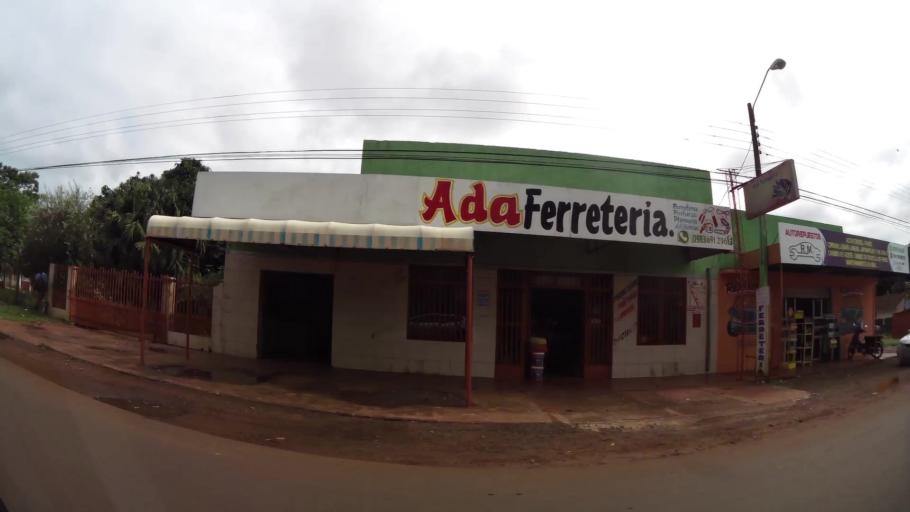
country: PY
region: Alto Parana
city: Ciudad del Este
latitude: -25.3947
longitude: -54.6401
